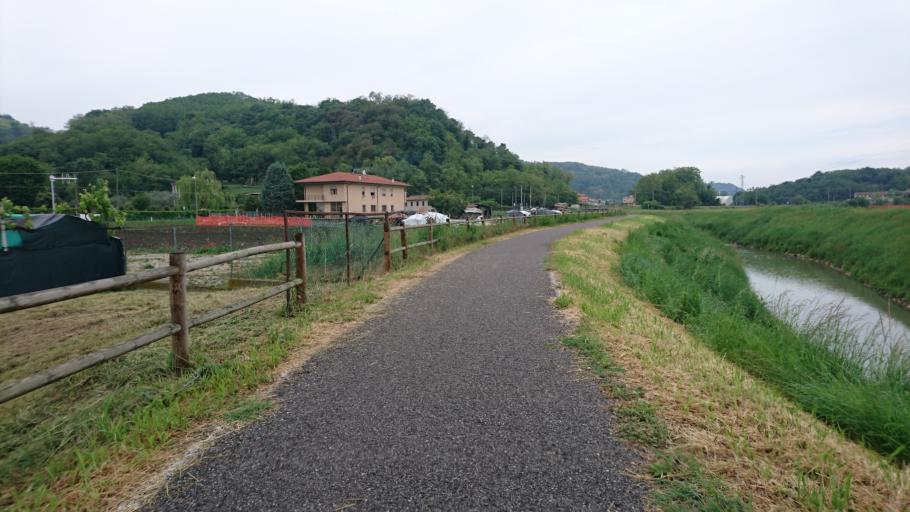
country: IT
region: Veneto
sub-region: Provincia di Padova
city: Montegrotto Terme
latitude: 45.3106
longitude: 11.7906
